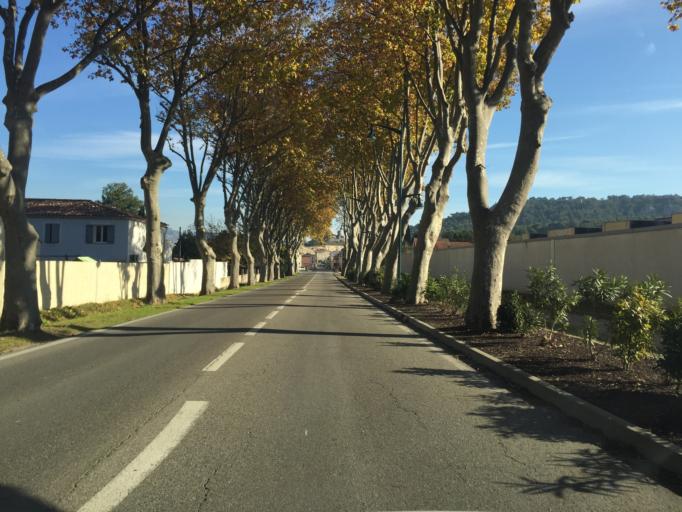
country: FR
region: Provence-Alpes-Cote d'Azur
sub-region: Departement des Bouches-du-Rhone
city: Orgon
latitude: 43.7920
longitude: 5.0315
